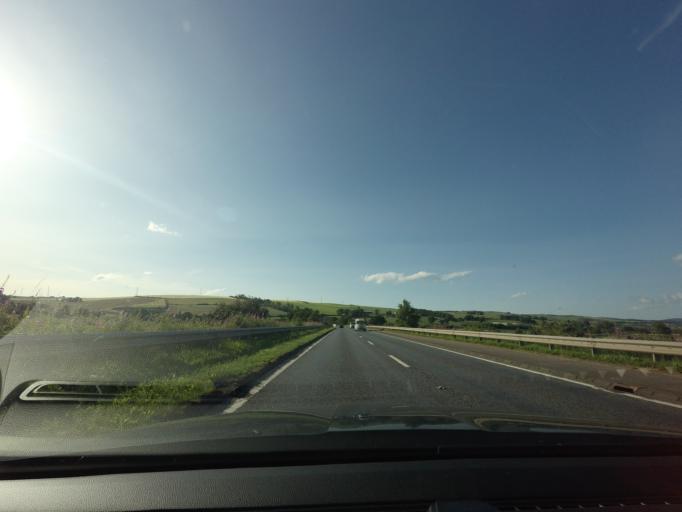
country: GB
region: Scotland
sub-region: Highland
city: Conon Bridge
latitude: 57.5762
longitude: -4.4331
